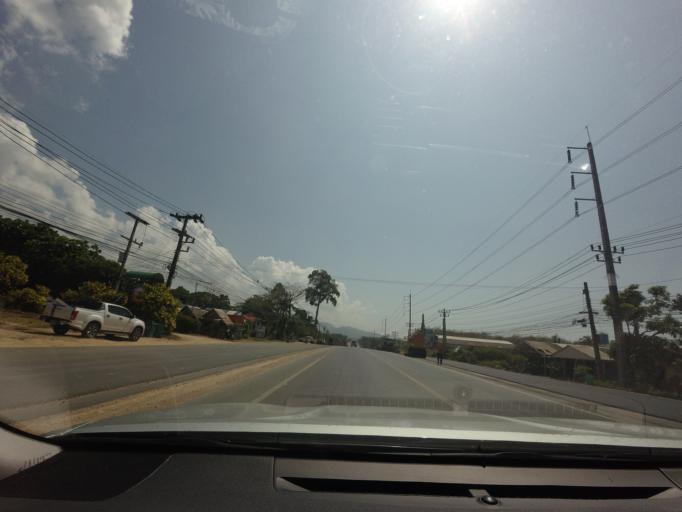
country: TH
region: Phangnga
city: Ban Khao Lak
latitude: 8.7226
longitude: 98.2564
